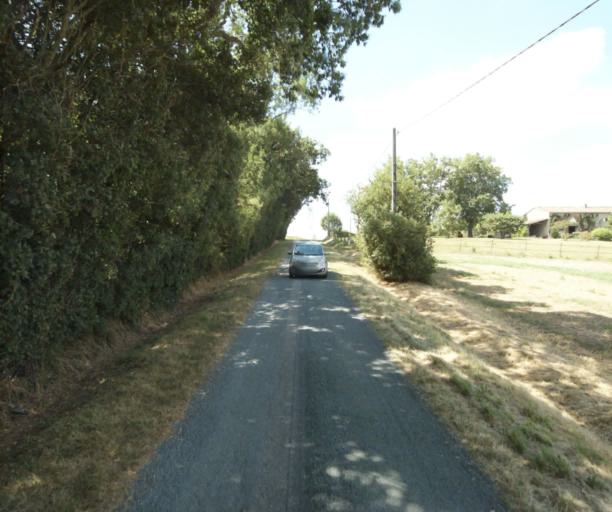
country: FR
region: Midi-Pyrenees
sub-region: Departement de la Haute-Garonne
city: Auriac-sur-Vendinelle
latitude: 43.4736
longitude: 1.8060
